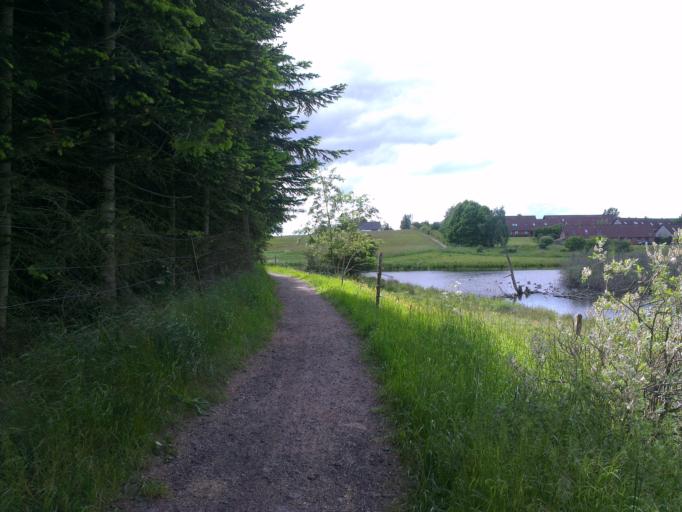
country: DK
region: Capital Region
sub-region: Frederikssund Kommune
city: Slangerup
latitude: 55.8501
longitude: 12.1867
